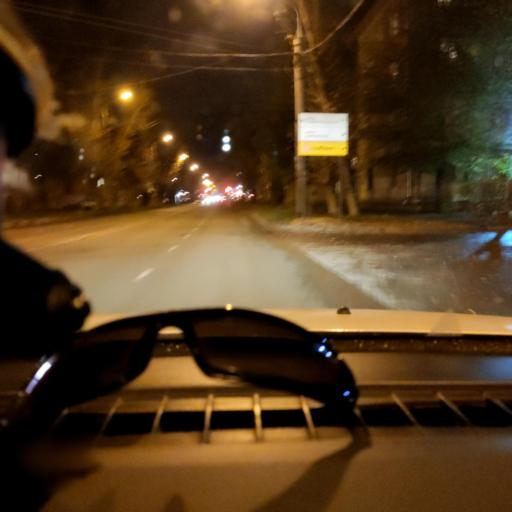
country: RU
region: Samara
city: Samara
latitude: 53.2268
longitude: 50.2569
